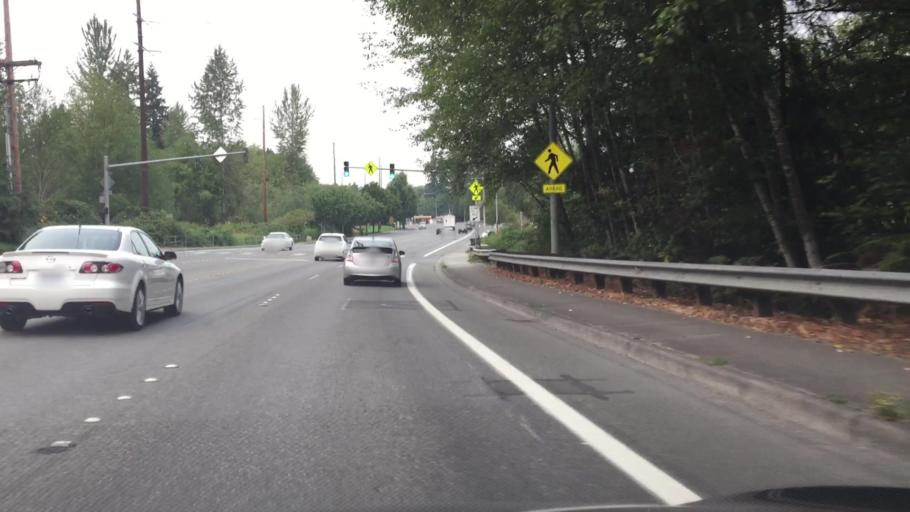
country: US
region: Washington
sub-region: King County
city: Redmond
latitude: 47.6986
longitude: -122.0932
